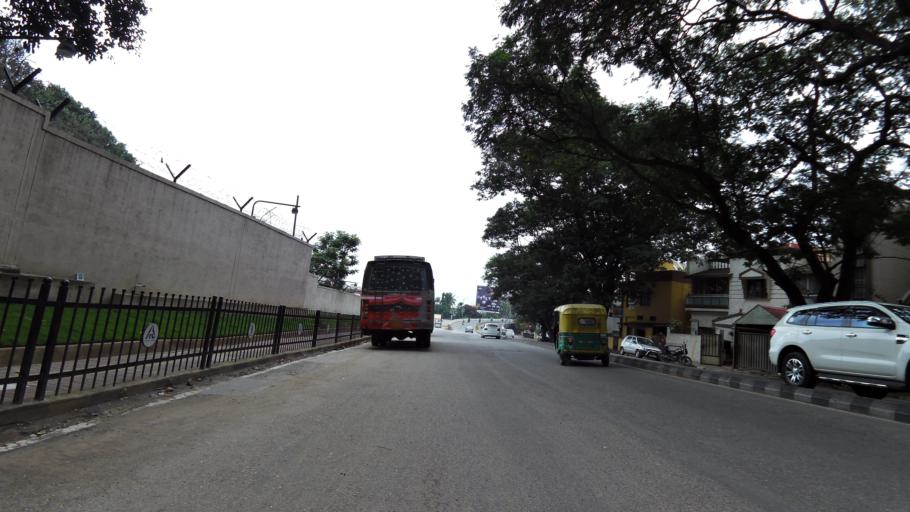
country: IN
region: Karnataka
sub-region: Bangalore Urban
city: Bangalore
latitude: 12.9990
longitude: 77.6245
